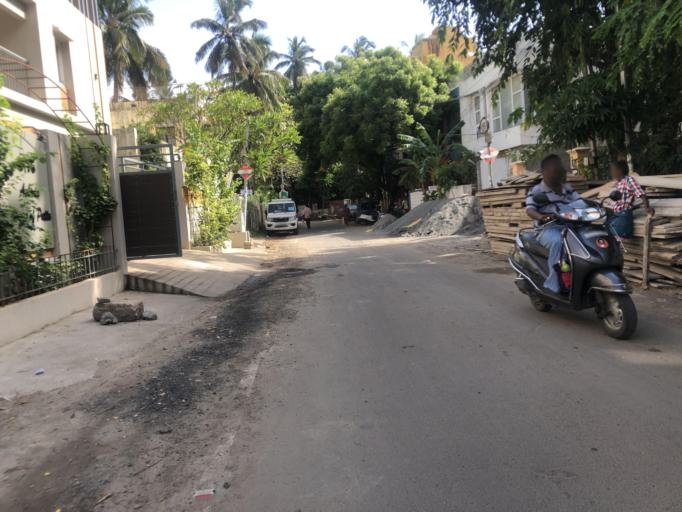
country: IN
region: Tamil Nadu
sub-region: Chennai
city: Gandhi Nagar
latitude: 13.0349
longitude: 80.2588
